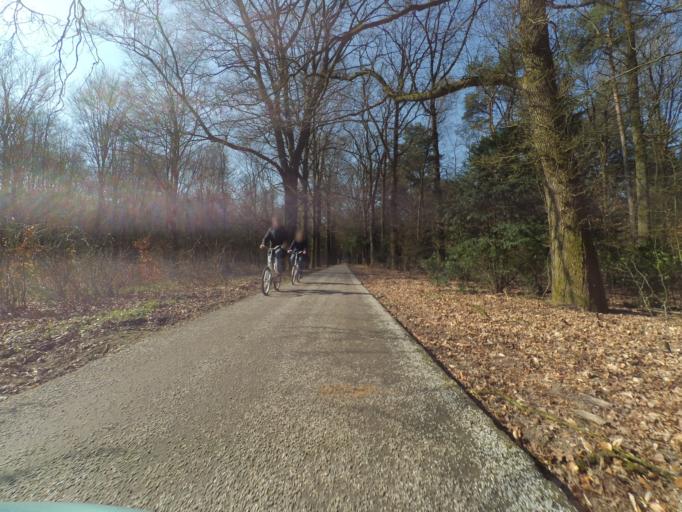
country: NL
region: Gelderland
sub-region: Gemeente Ede
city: Otterlo
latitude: 52.1024
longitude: 5.8385
